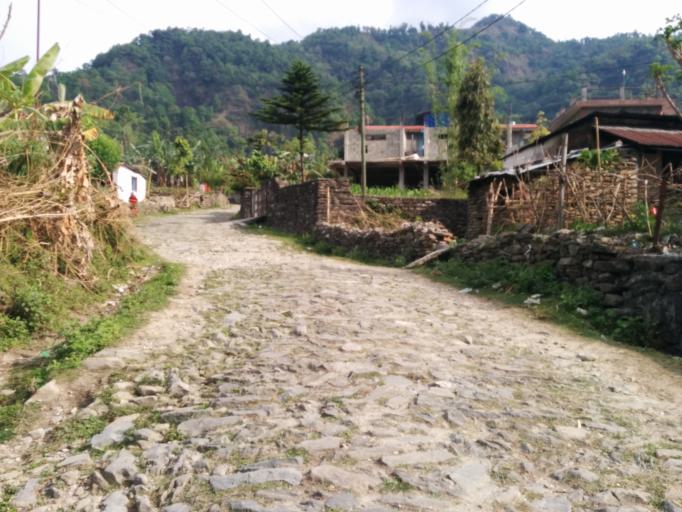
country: NP
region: Western Region
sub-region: Gandaki Zone
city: Pokhara
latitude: 28.2274
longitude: 83.9499
